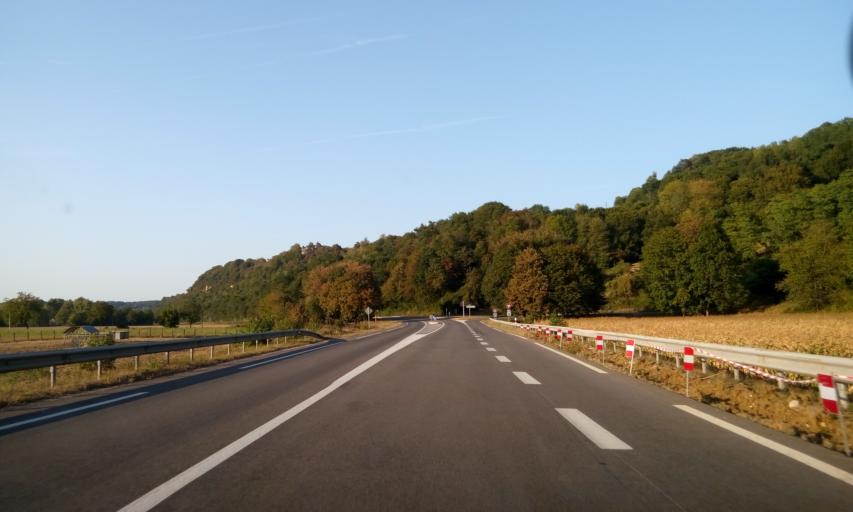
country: FR
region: Rhone-Alpes
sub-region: Departement de l'Ain
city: Neuville-sur-Ain
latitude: 46.0565
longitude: 5.3855
